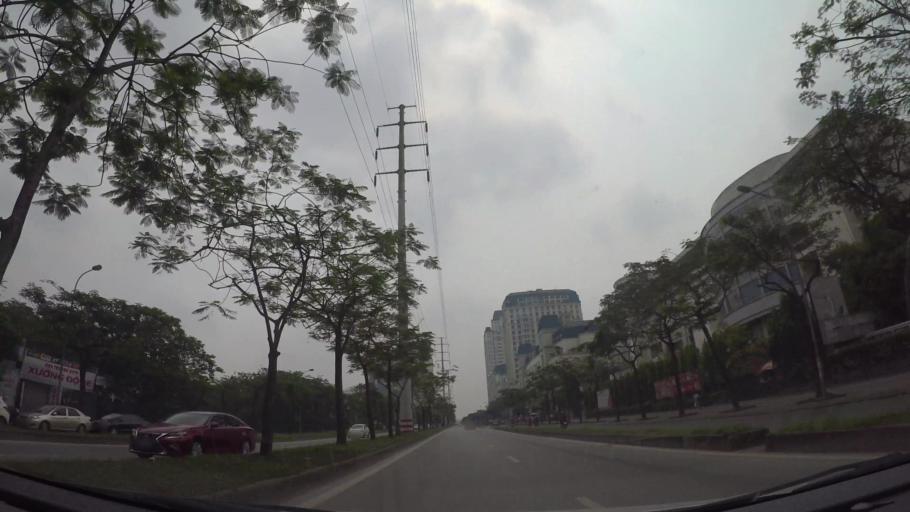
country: VN
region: Ha Noi
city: Cau Giay
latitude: 21.0159
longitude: 105.7796
